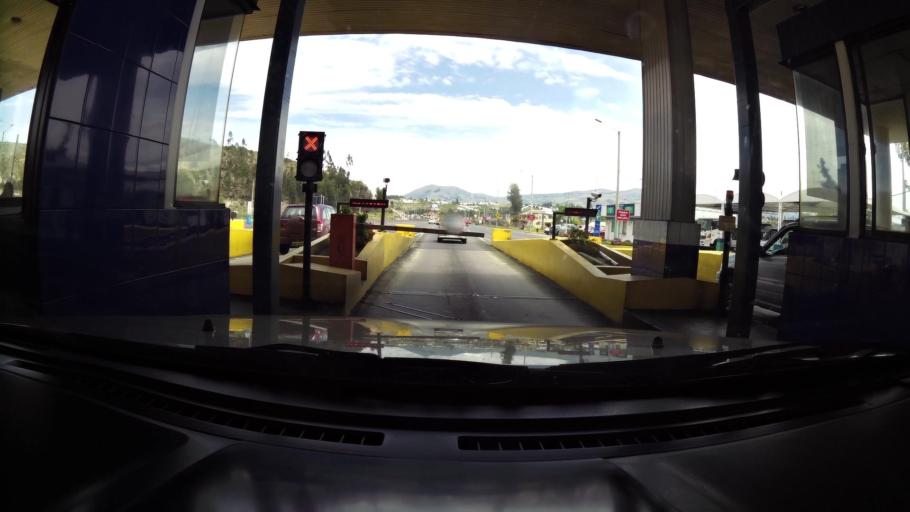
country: EC
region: Cotopaxi
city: San Miguel de Salcedo
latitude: -1.0593
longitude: -78.6017
